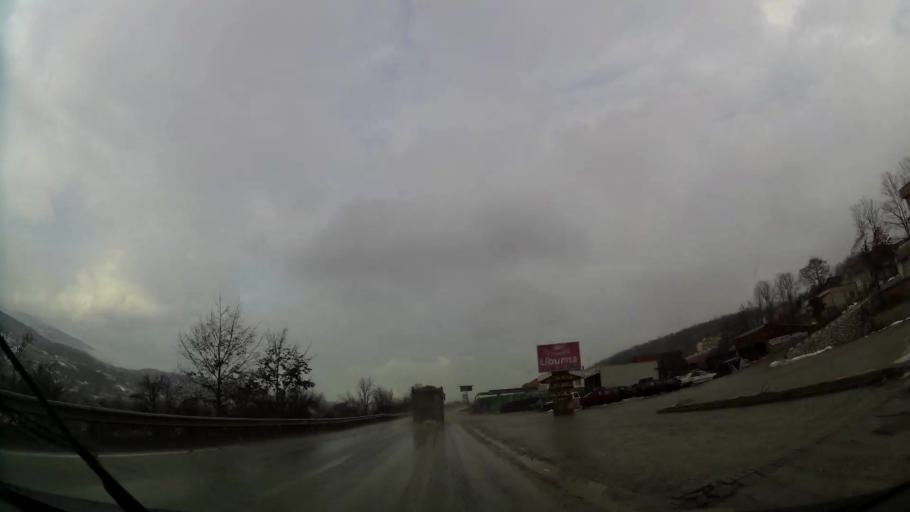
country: XK
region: Ferizaj
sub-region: Komuna e Kacanikut
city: Kacanik
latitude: 42.2391
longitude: 21.2451
